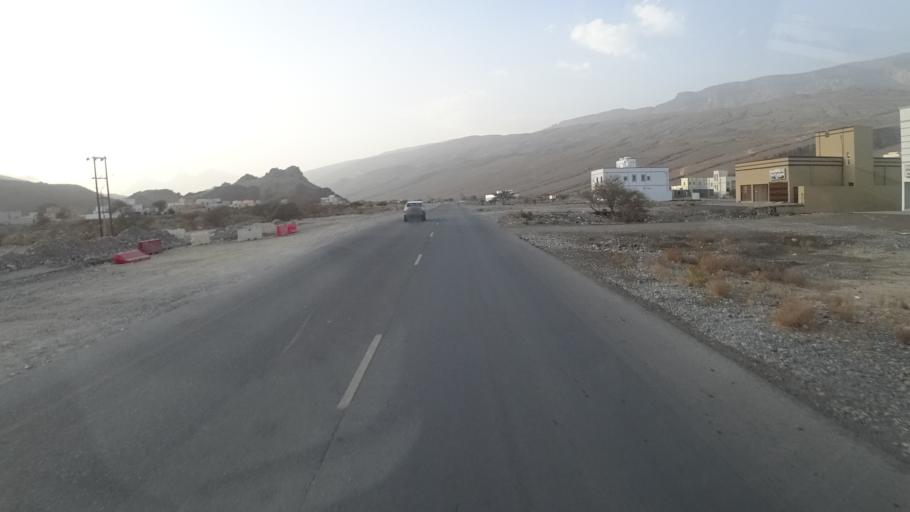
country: OM
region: Muhafazat ad Dakhiliyah
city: Bahla'
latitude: 23.1211
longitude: 57.2605
